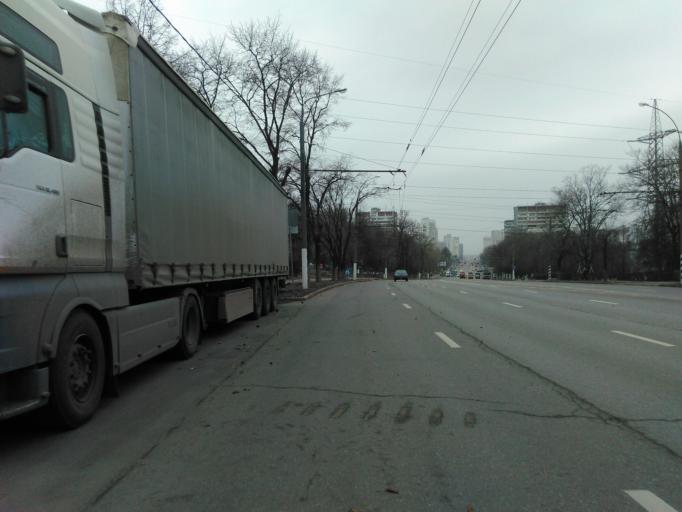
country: RU
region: Moscow
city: Zyuzino
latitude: 55.6517
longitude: 37.5855
